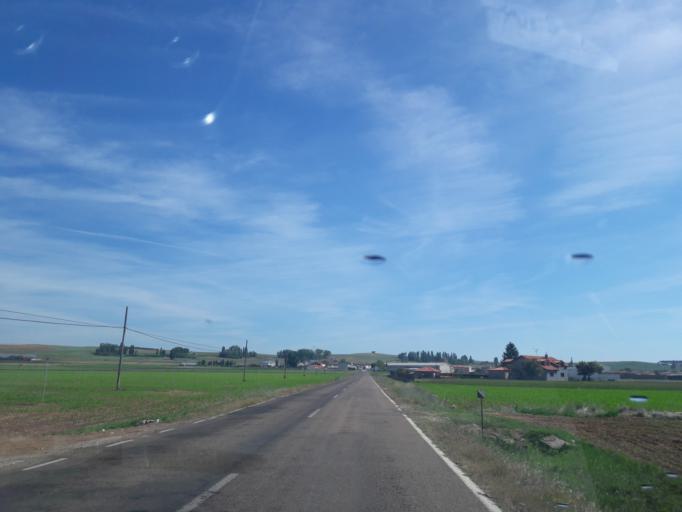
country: ES
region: Castille and Leon
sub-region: Provincia de Salamanca
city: Villoruela
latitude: 40.9995
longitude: -5.4002
